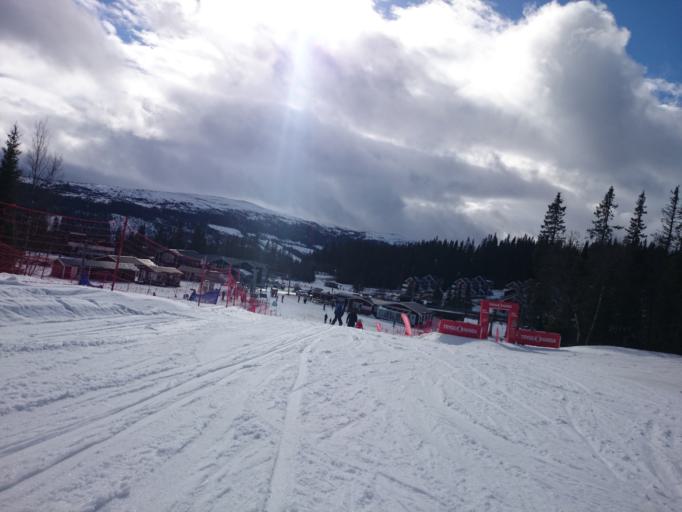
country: SE
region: Jaemtland
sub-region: Are Kommun
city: Are
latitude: 63.3894
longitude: 13.1556
